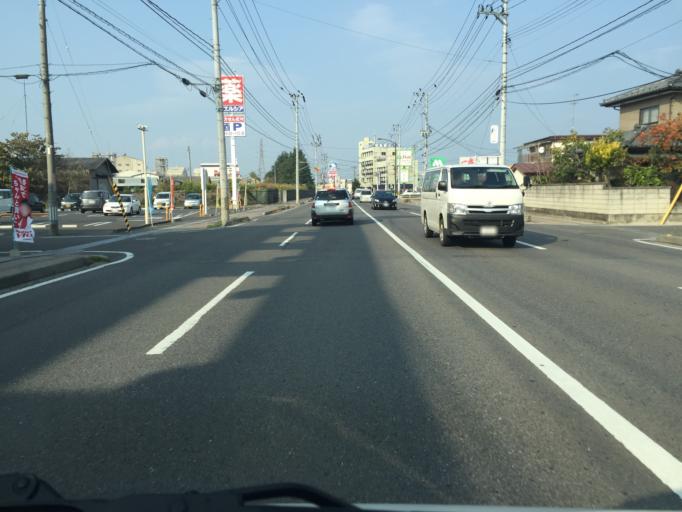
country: JP
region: Fukushima
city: Koriyama
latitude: 37.3958
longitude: 140.3956
